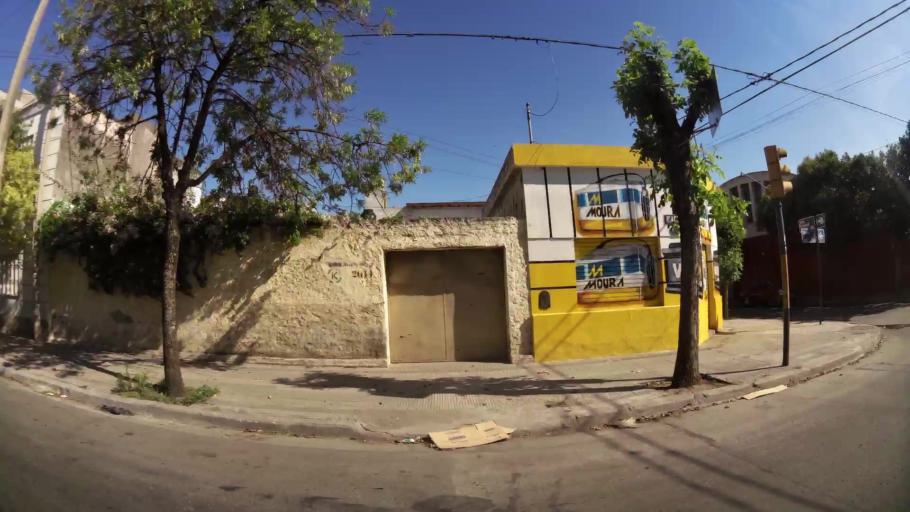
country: AR
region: Cordoba
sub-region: Departamento de Capital
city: Cordoba
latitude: -31.4044
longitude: -64.1567
